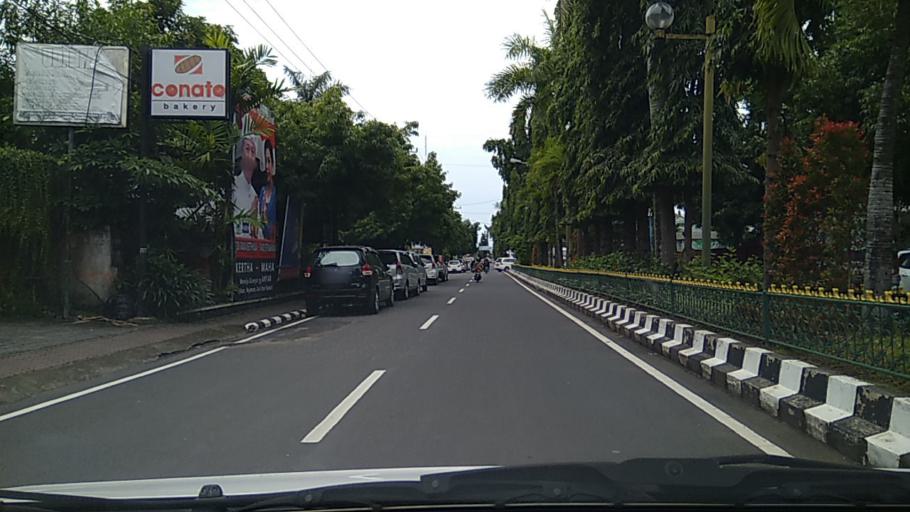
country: ID
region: Bali
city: Banjar Kelodan
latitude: -8.5378
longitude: 115.3228
